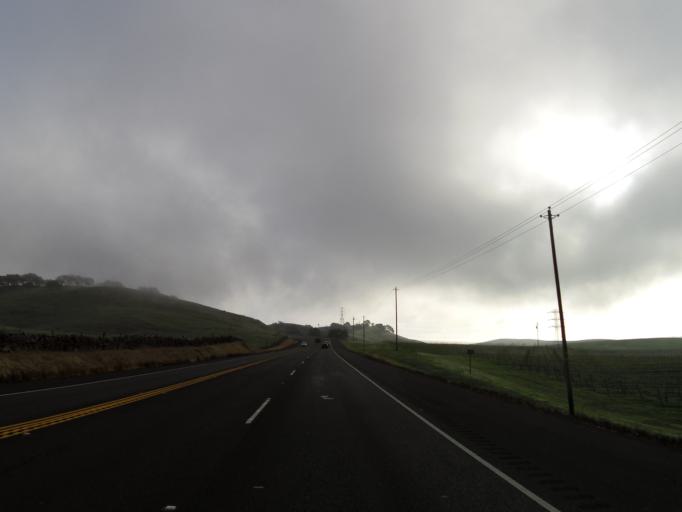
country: US
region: California
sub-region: Sonoma County
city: Sonoma
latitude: 38.2513
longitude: -122.3853
